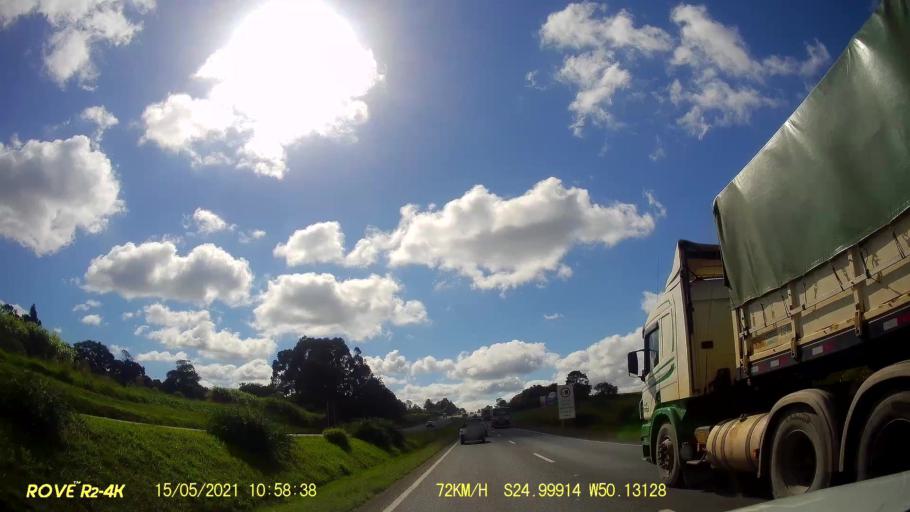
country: BR
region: Parana
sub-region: Carambei
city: Carambei
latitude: -24.9993
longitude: -50.1314
